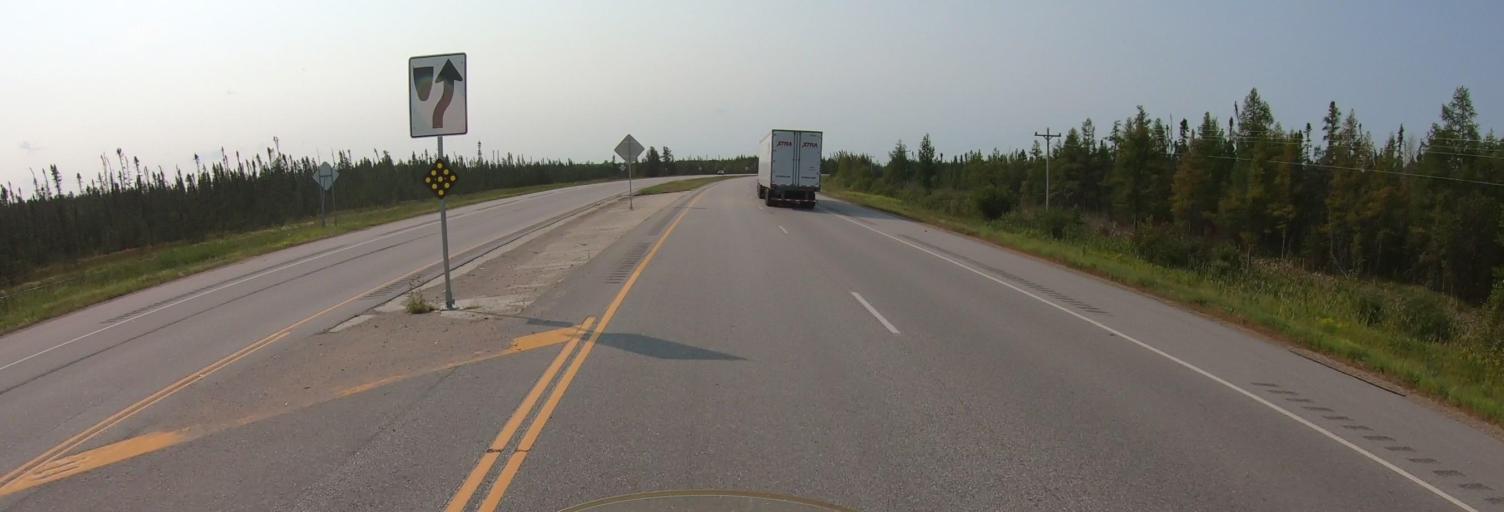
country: US
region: Minnesota
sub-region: Saint Louis County
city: Mountain Iron
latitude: 47.8409
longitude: -92.6767
